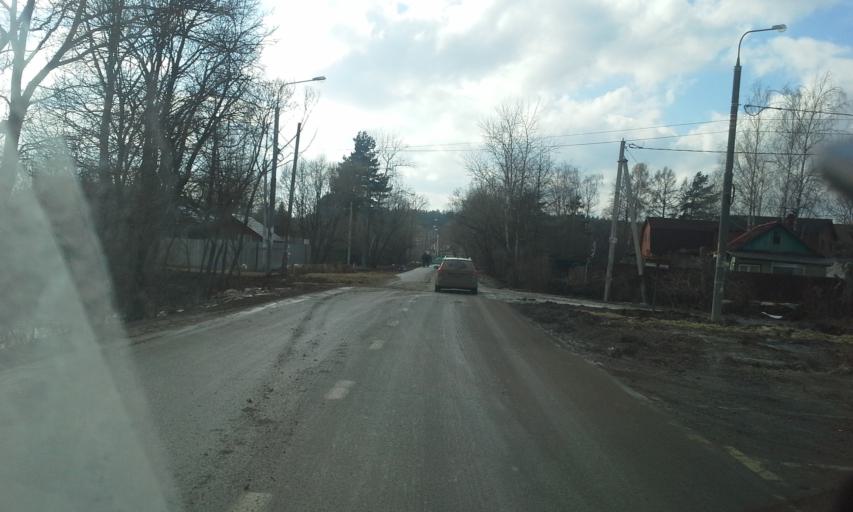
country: RU
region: Moscow
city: Tolstopal'tsevo
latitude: 55.6109
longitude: 37.2060
